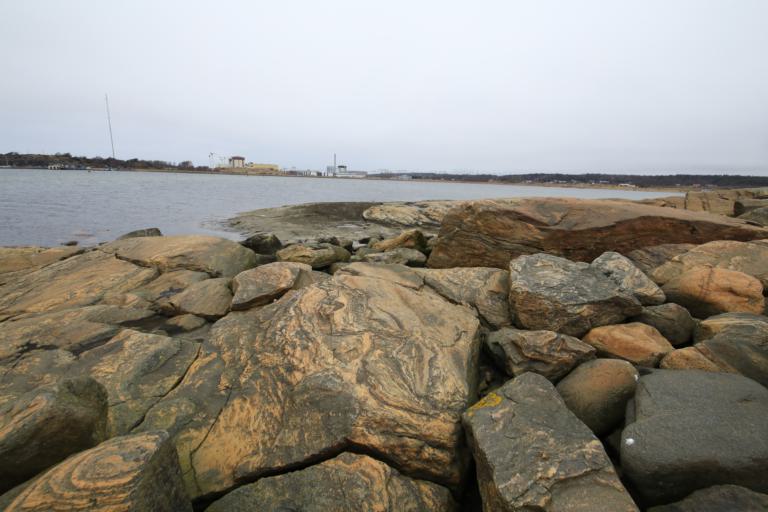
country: SE
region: Halland
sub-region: Kungsbacka Kommun
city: Frillesas
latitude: 57.2471
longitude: 12.1179
